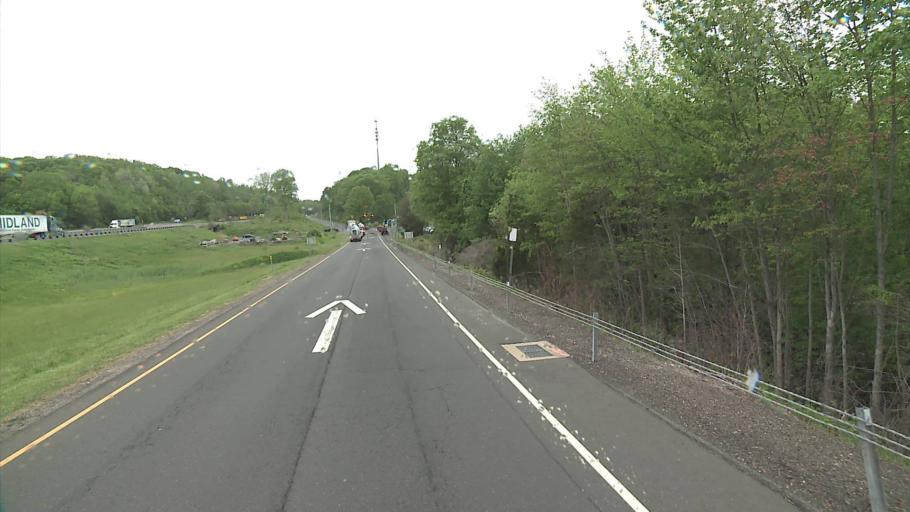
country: US
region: Connecticut
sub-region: New Haven County
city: Middlebury
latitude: 41.4954
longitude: -73.1609
